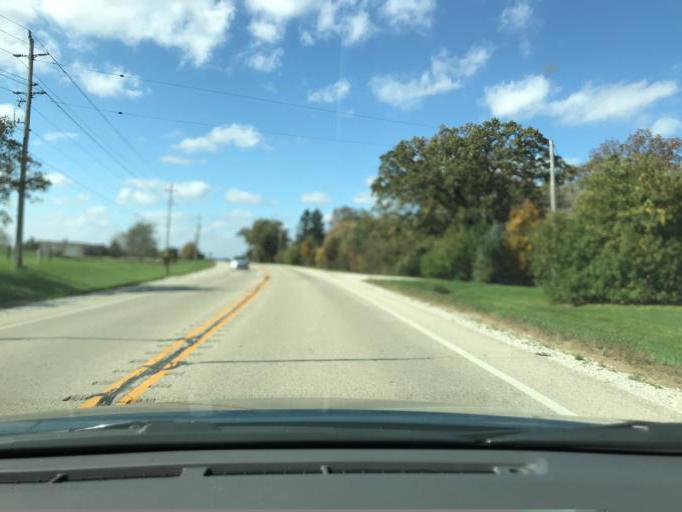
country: US
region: Wisconsin
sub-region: Racine County
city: Union Grove
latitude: 42.6278
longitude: -88.0063
